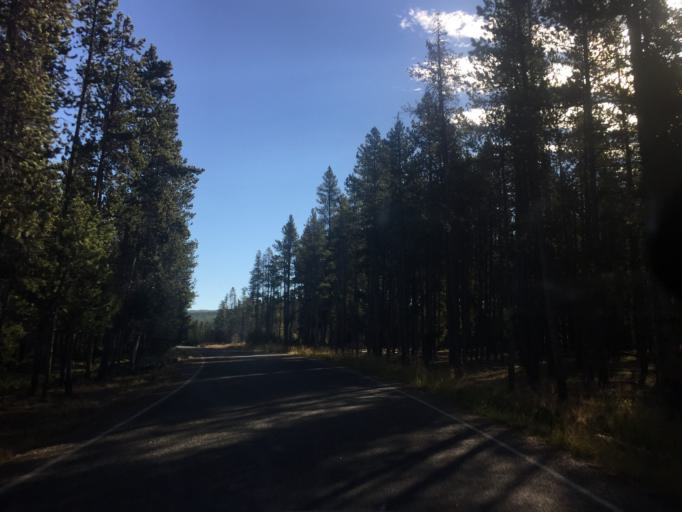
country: US
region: Montana
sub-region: Gallatin County
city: West Yellowstone
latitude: 44.5353
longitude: -110.8103
